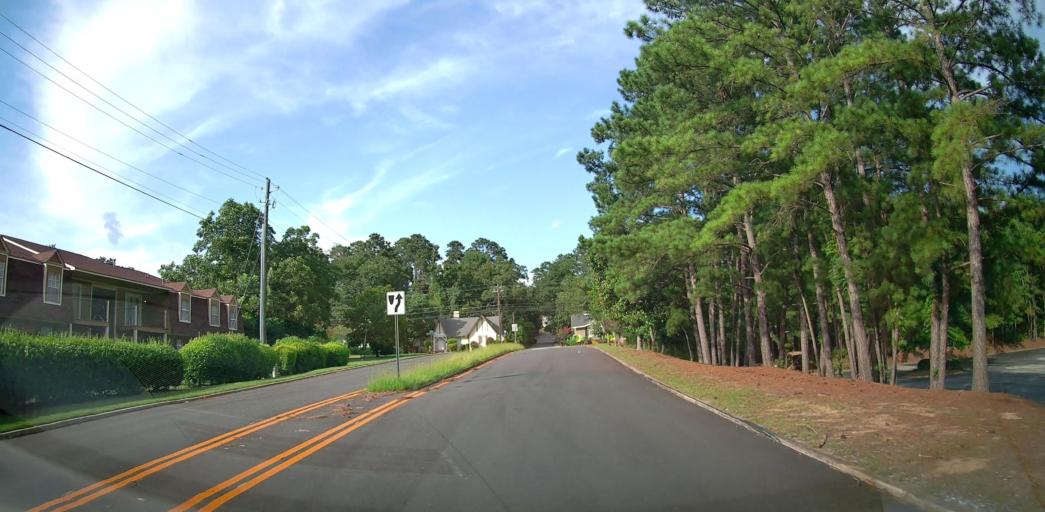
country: US
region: Georgia
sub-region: Bibb County
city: Macon
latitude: 32.8518
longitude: -83.6272
